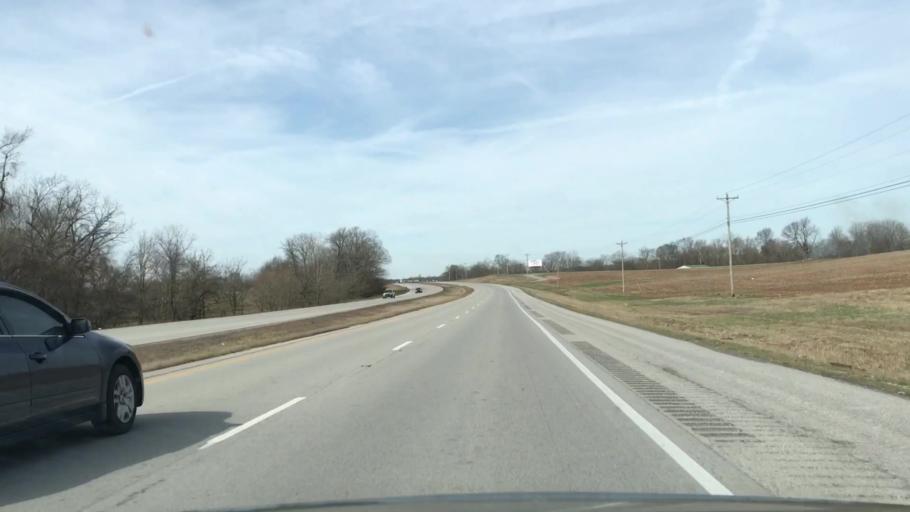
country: US
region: Kentucky
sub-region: Christian County
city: Hopkinsville
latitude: 36.8811
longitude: -87.5979
